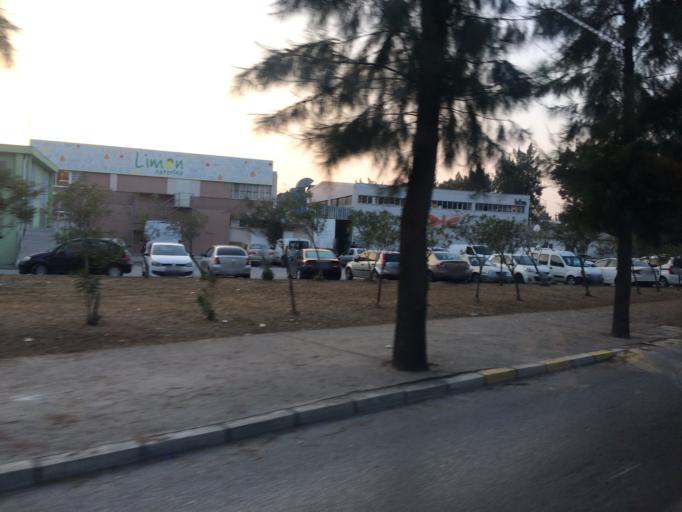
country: TR
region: Izmir
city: Karsiyaka
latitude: 38.4946
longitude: 27.0462
